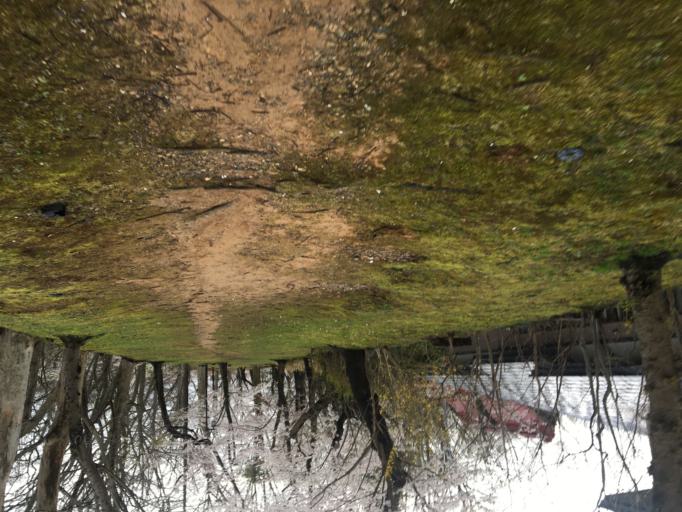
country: JP
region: Akita
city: Akita
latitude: 39.7222
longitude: 140.1230
